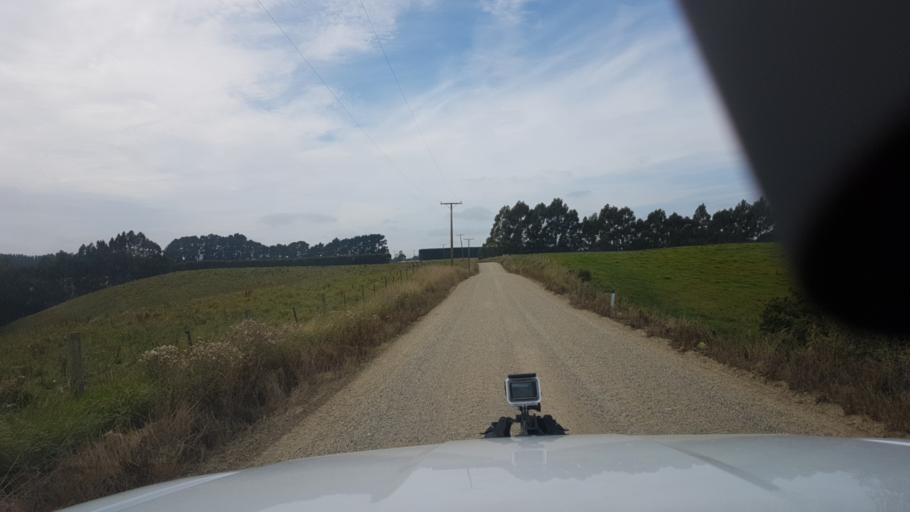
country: NZ
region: Otago
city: Oamaru
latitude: -45.0495
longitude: 170.9729
